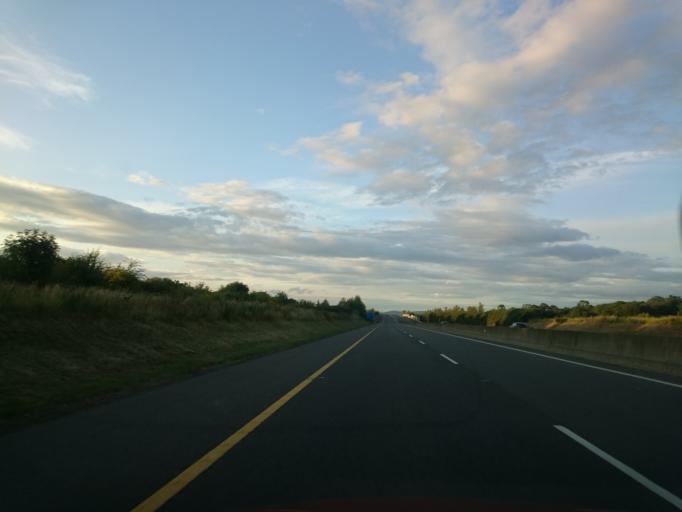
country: IE
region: Leinster
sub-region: Loch Garman
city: Castletown
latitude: 52.7192
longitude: -6.2474
